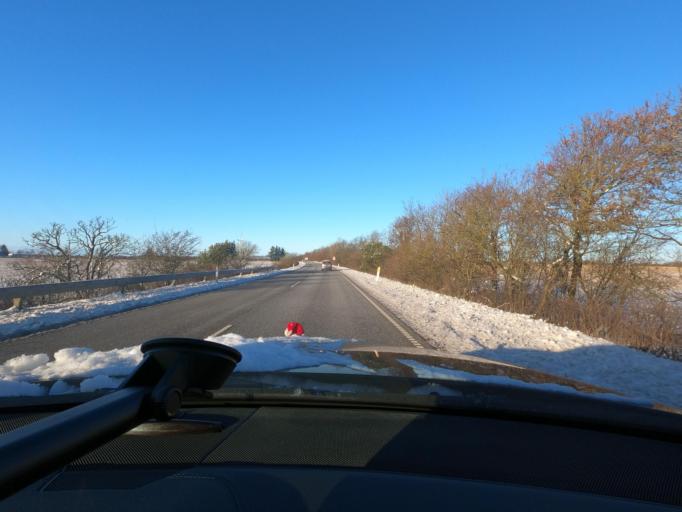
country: DK
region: South Denmark
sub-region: Aabenraa Kommune
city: Rodekro
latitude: 55.1053
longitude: 9.1839
